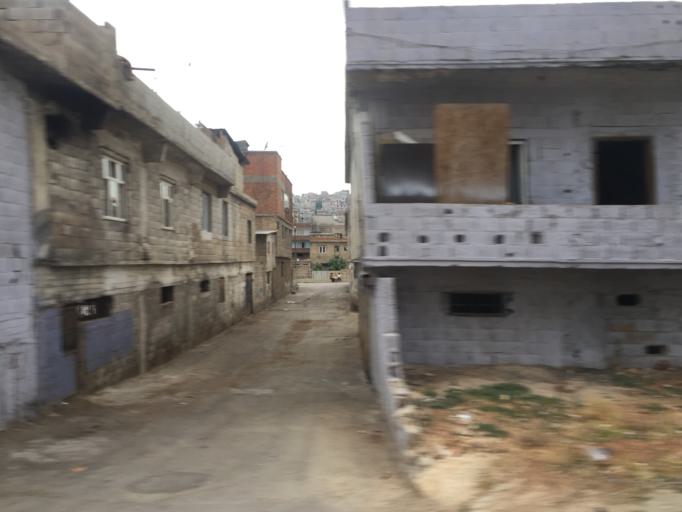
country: TR
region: Gaziantep
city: Gaziantep
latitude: 37.0716
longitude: 37.4133
